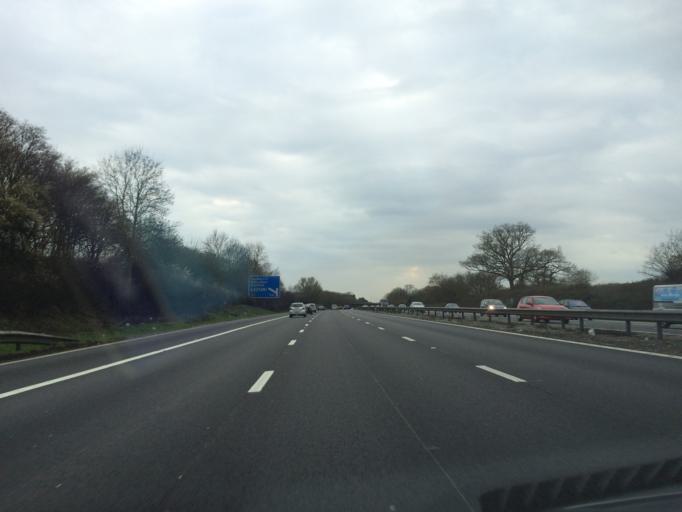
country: GB
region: England
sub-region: Wokingham
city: Wokingham
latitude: 51.4405
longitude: -0.8323
